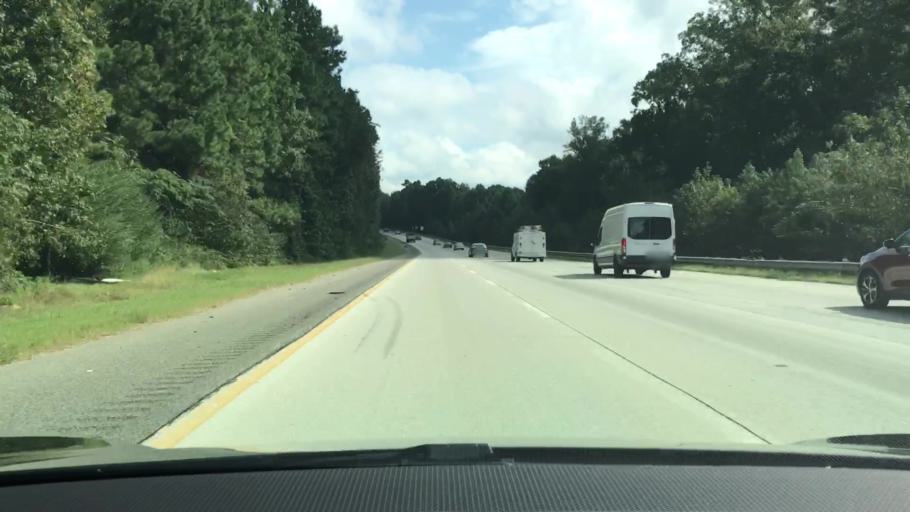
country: US
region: Georgia
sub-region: Hall County
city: Oakwood
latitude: 34.2342
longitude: -83.8466
